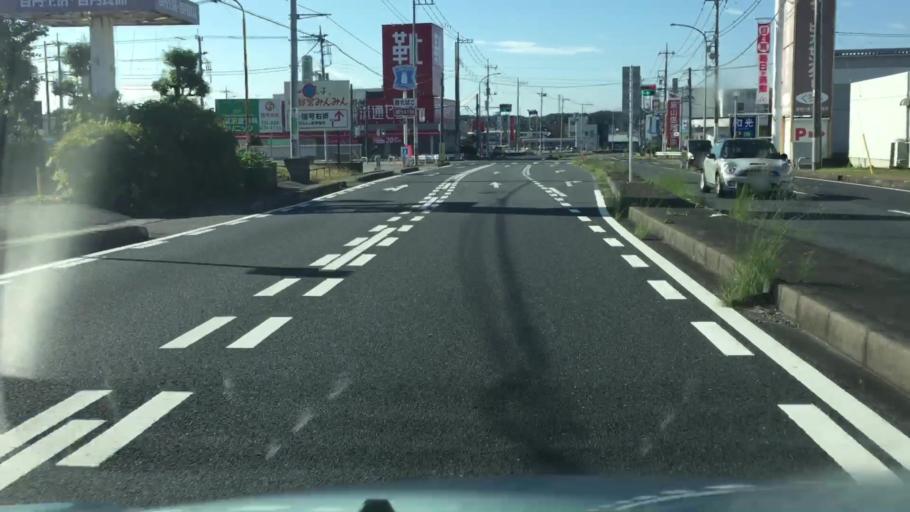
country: JP
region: Tochigi
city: Ujiie
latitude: 36.6217
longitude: 139.9920
